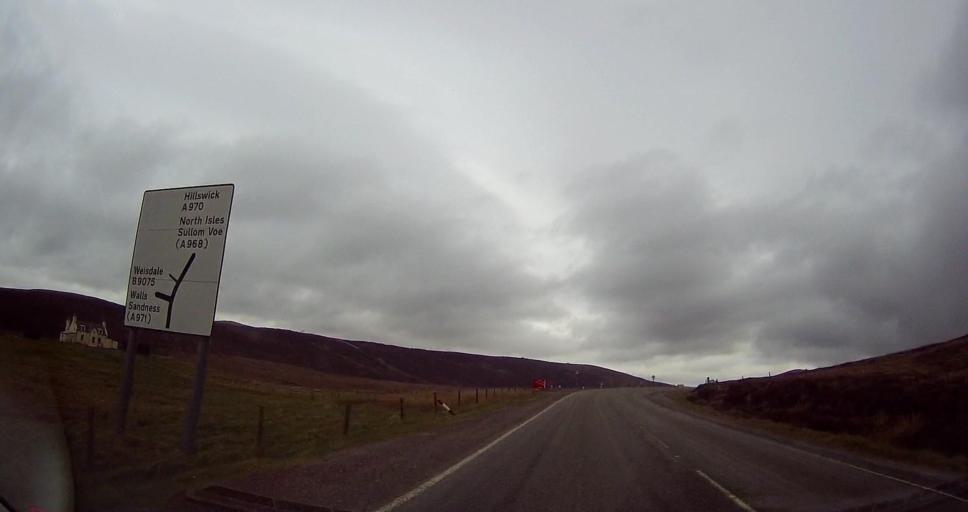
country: GB
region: Scotland
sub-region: Shetland Islands
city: Lerwick
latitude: 60.2776
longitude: -1.2439
